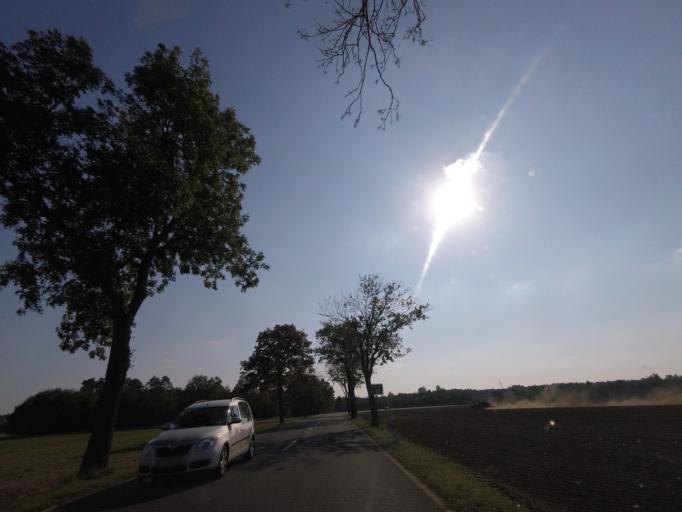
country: DE
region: Saxony-Anhalt
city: Jessen
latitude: 51.8256
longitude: 13.0154
